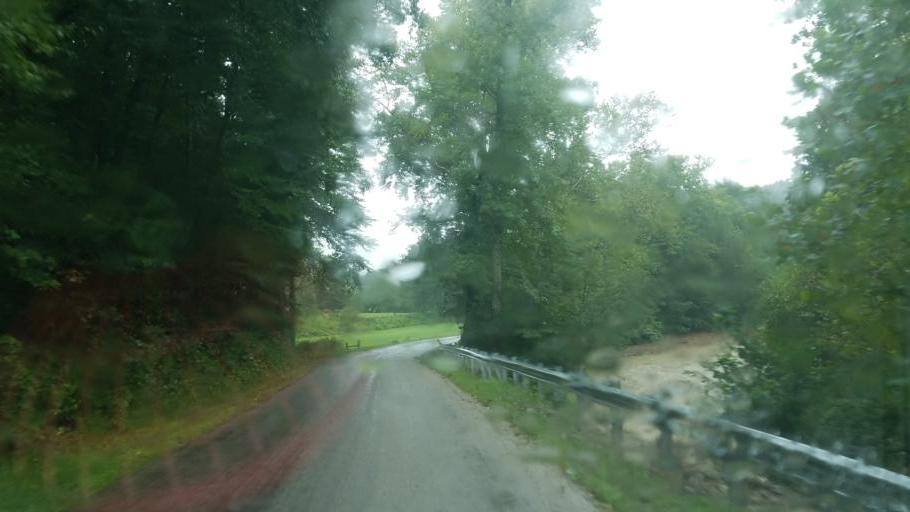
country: US
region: Ohio
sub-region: Adams County
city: Peebles
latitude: 38.8180
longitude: -83.2394
